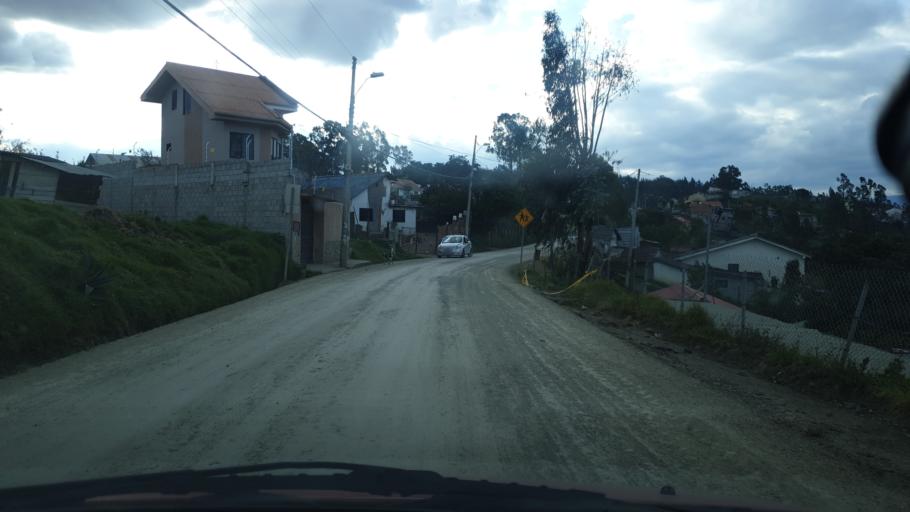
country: EC
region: Azuay
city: Cuenca
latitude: -2.9231
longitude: -78.9740
